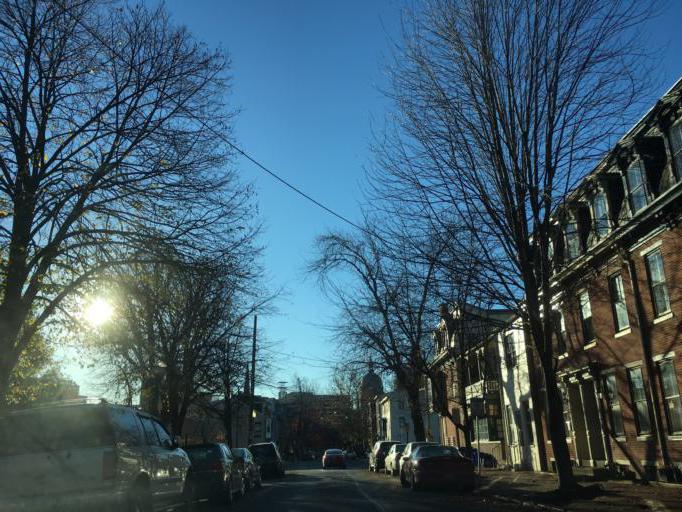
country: US
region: Pennsylvania
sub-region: Dauphin County
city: Harrisburg
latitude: 40.2665
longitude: -76.8883
